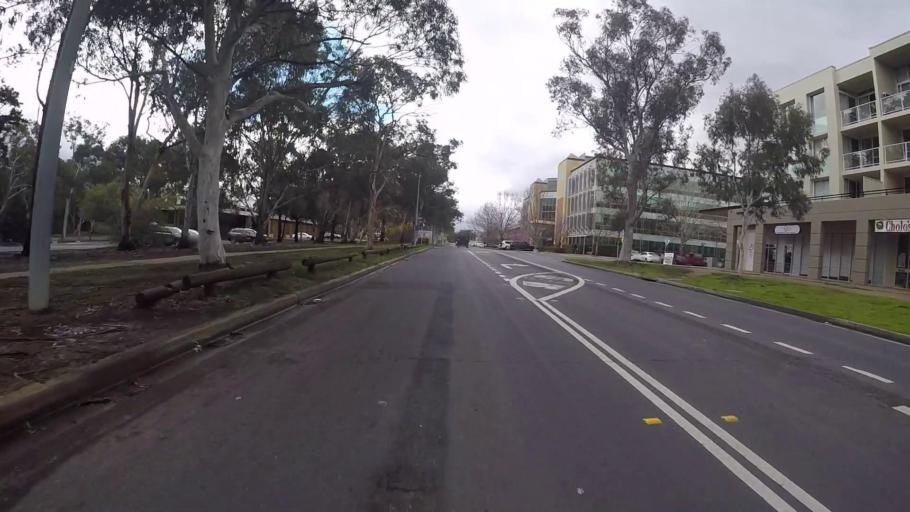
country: AU
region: Australian Capital Territory
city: Acton
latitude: -35.2515
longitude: 149.1352
